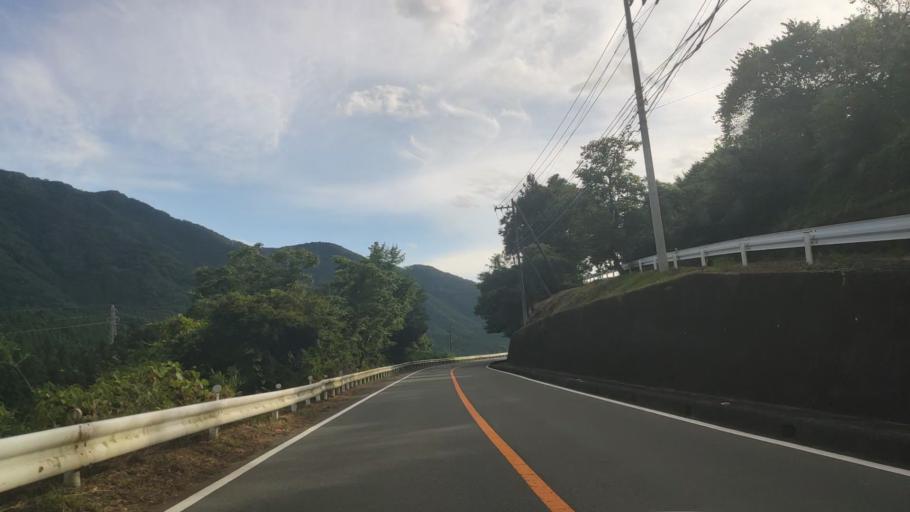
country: JP
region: Gunma
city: Omamacho-omama
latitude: 36.5325
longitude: 139.3323
